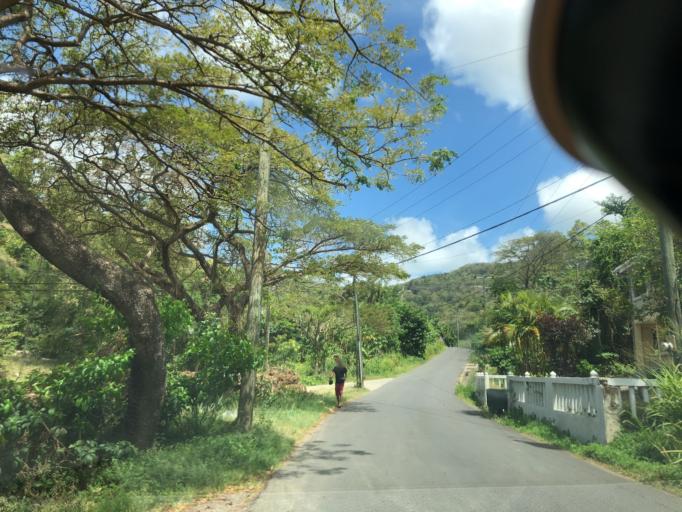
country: LC
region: Gros-Islet
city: Gros Islet
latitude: 14.0569
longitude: -60.9655
